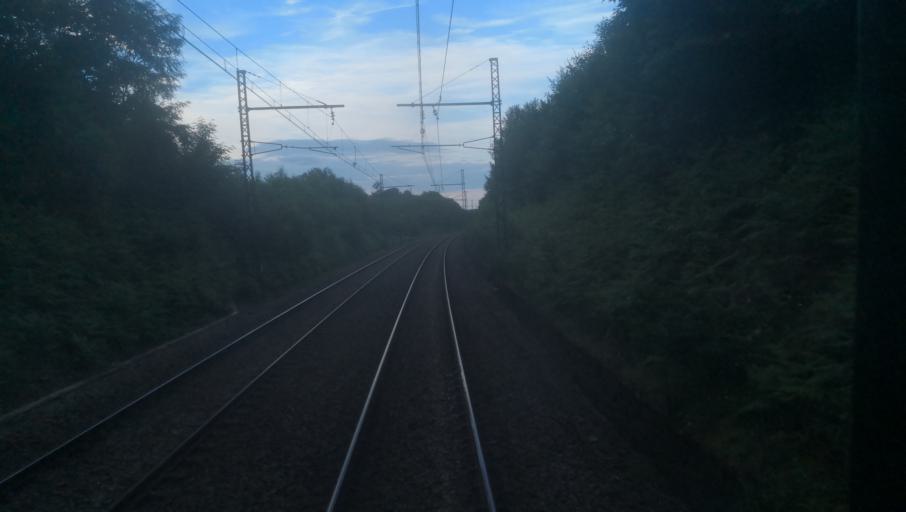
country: FR
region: Limousin
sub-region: Departement de la Creuse
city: Saint-Maurice-la-Souterraine
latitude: 46.1739
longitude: 1.4364
